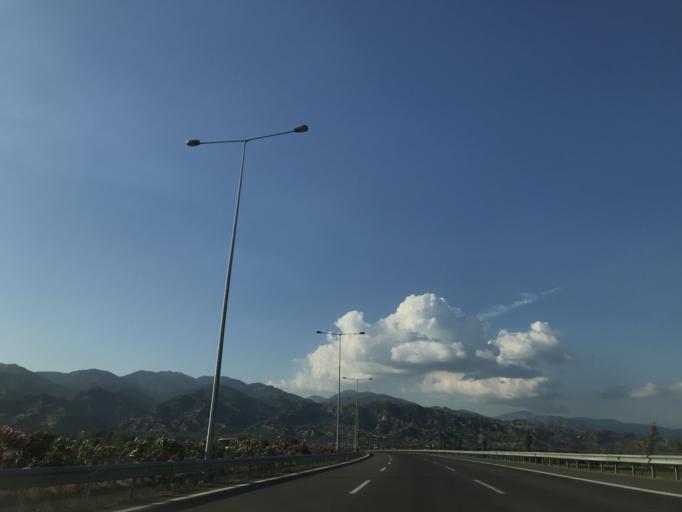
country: TR
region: Aydin
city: Tepecik
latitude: 37.8299
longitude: 27.9177
